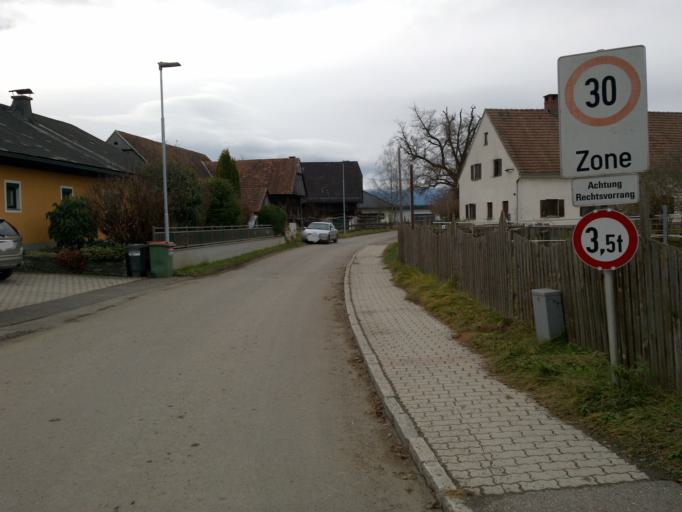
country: AT
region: Styria
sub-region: Politischer Bezirk Murtal
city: Apfelberg
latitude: 47.2028
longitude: 14.8346
